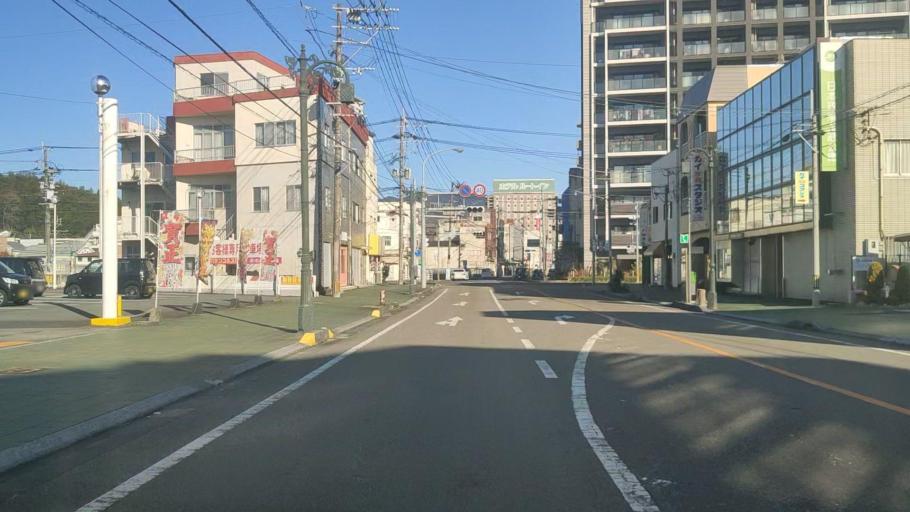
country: JP
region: Miyazaki
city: Nobeoka
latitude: 32.5860
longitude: 131.6712
